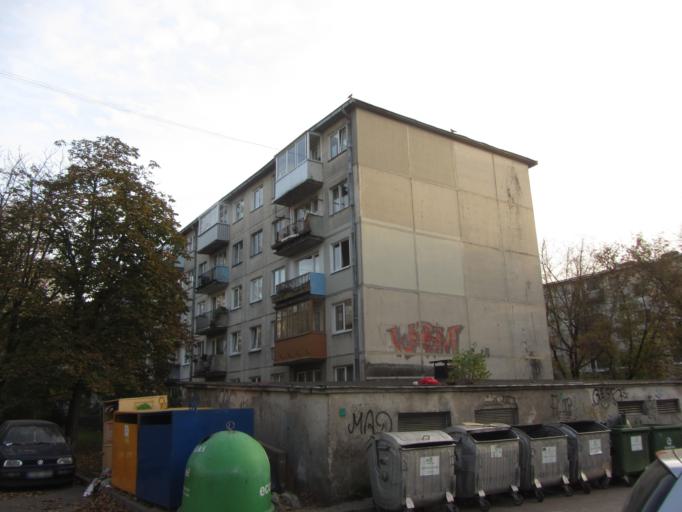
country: LT
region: Vilnius County
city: Vilkpede
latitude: 54.6753
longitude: 25.2476
